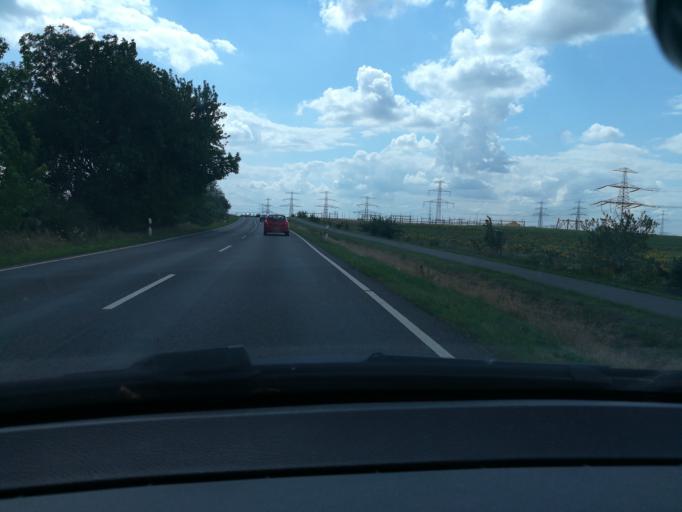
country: DE
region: Saxony-Anhalt
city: Zielitz
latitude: 52.2746
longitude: 11.6496
